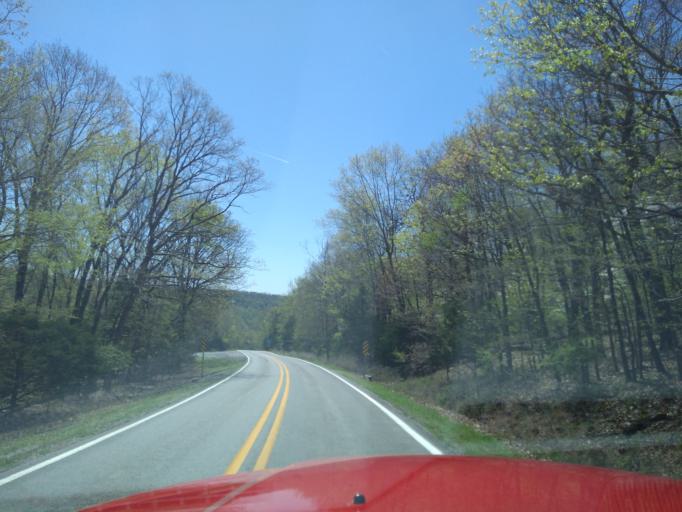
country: US
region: Arkansas
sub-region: Washington County
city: West Fork
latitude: 35.7826
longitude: -94.2580
